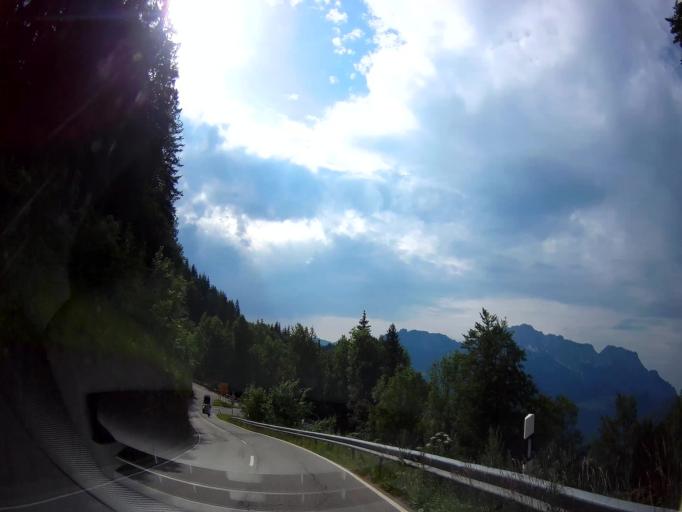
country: DE
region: Bavaria
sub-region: Upper Bavaria
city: Berchtesgaden
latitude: 47.6312
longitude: 13.0582
